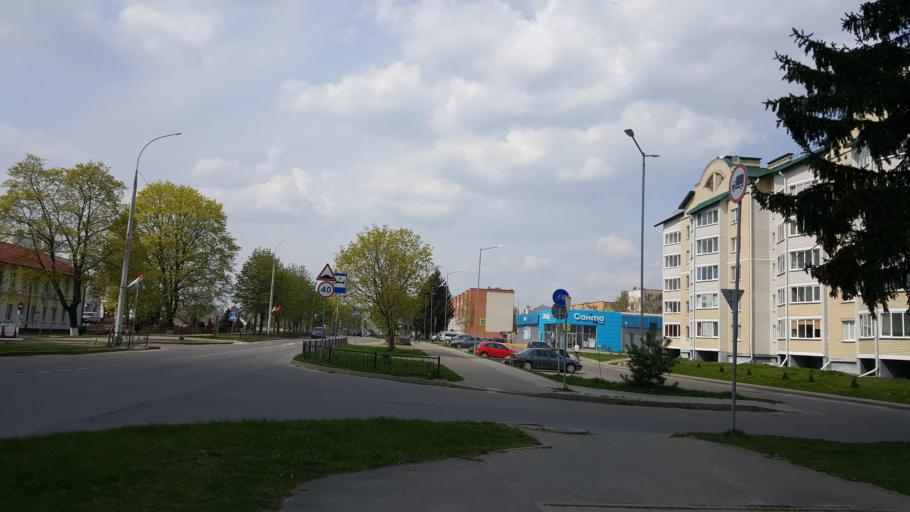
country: BY
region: Brest
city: Zhabinka
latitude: 52.1894
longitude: 24.0316
